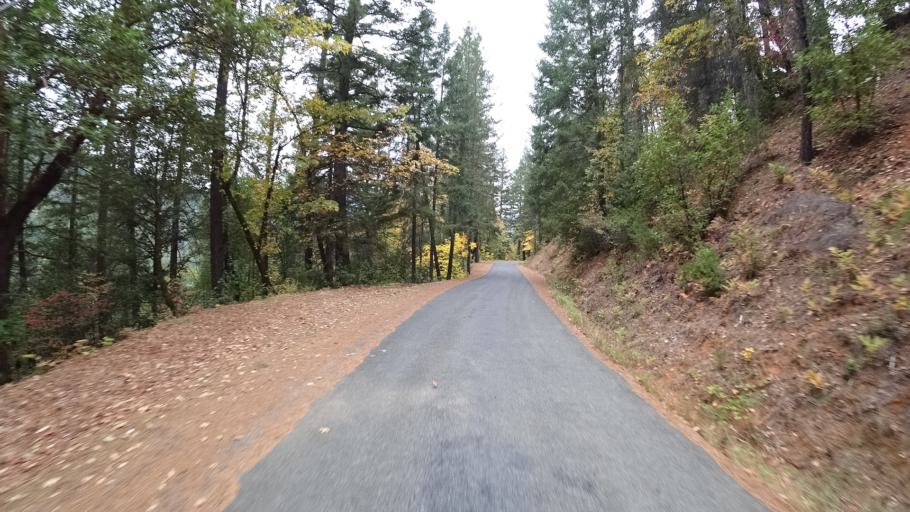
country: US
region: California
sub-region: Siskiyou County
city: Happy Camp
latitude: 41.7742
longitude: -123.3800
